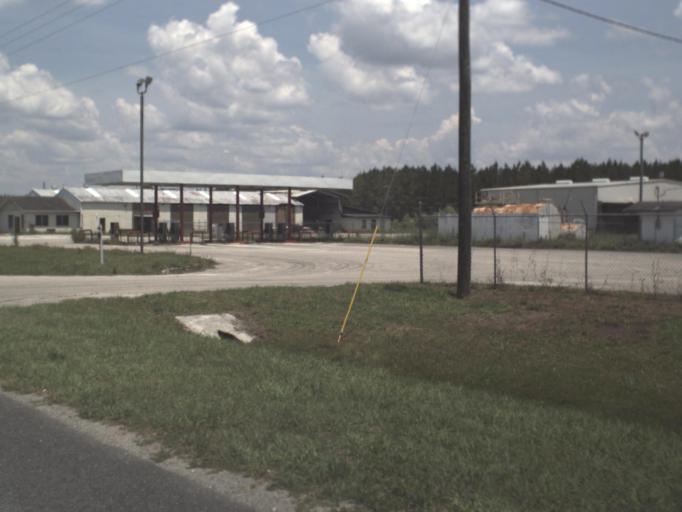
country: US
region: Florida
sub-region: Union County
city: Lake Butler
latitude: 30.0306
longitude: -82.3639
